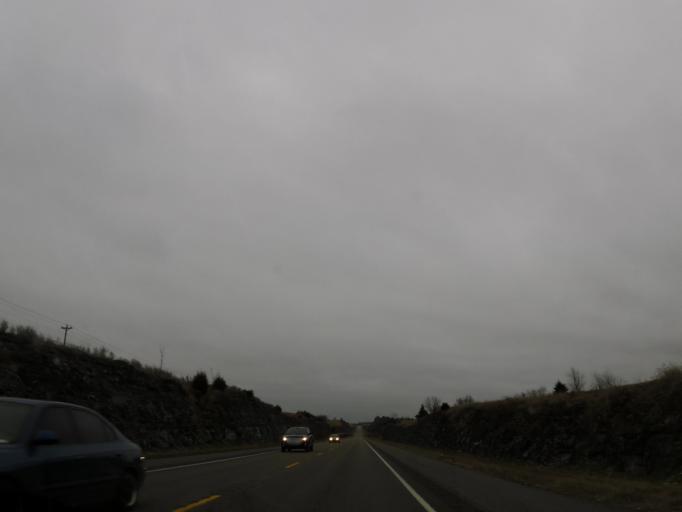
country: US
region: Kentucky
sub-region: Lincoln County
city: Stanford
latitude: 37.5091
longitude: -84.5893
